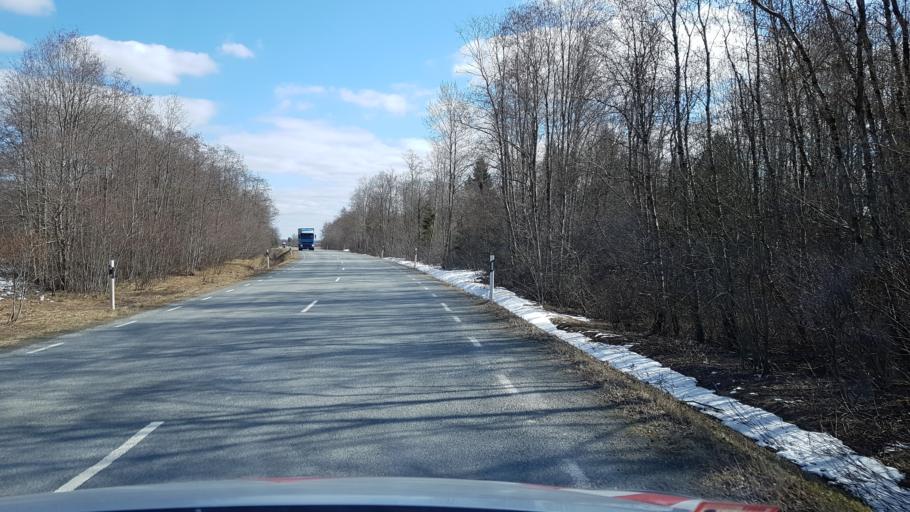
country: EE
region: Laeaene-Virumaa
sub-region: Tapa vald
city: Tapa
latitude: 59.2721
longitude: 25.9196
